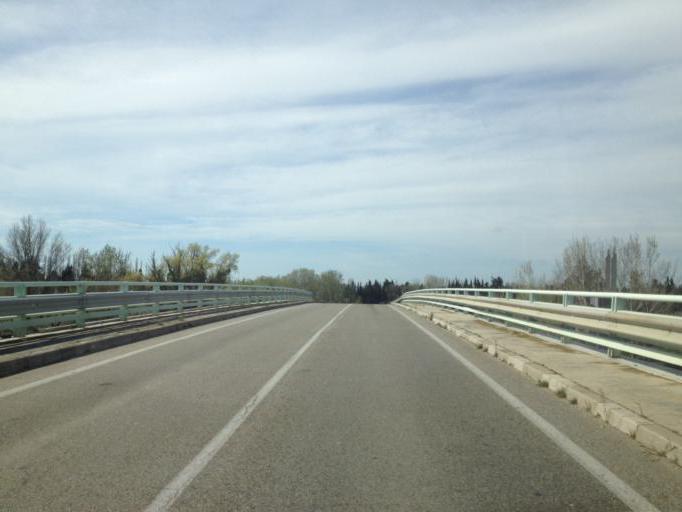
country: FR
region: Provence-Alpes-Cote d'Azur
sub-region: Departement du Vaucluse
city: Orange
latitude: 44.1351
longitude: 4.7851
